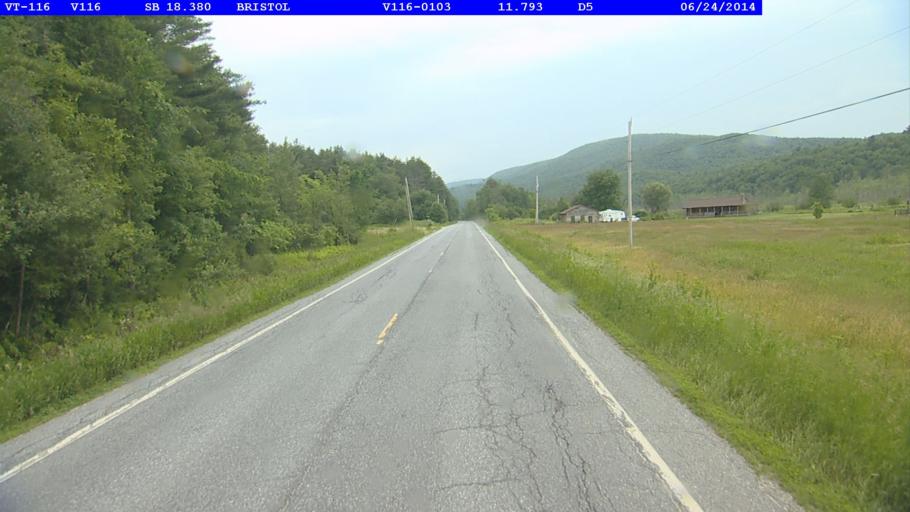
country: US
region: Vermont
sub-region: Addison County
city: Bristol
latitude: 44.1789
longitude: -73.0572
